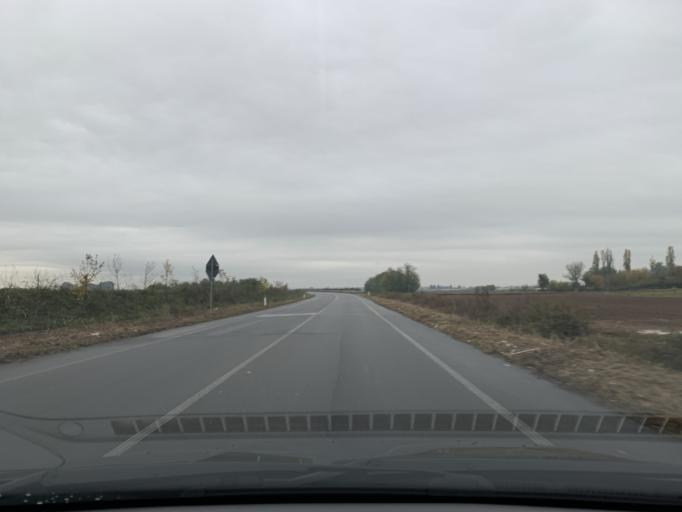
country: IT
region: Lombardy
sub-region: Provincia di Monza e Brianza
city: Ceriano Laghetto
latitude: 45.6306
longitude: 9.0605
